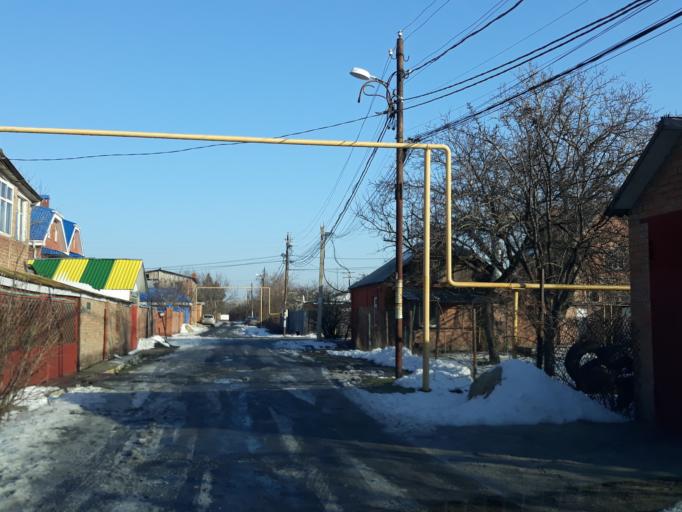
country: RU
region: Rostov
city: Taganrog
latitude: 47.2406
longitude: 38.8722
